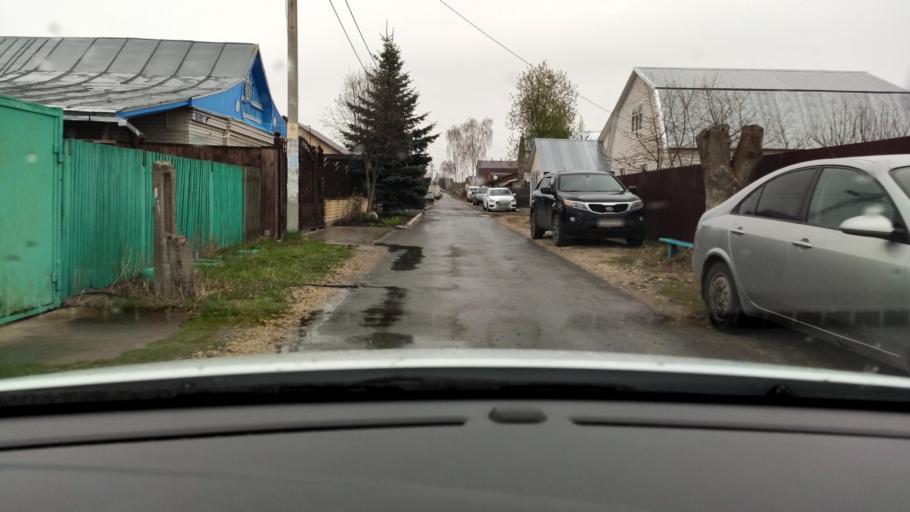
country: RU
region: Tatarstan
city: Osinovo
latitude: 55.8286
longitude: 48.8652
